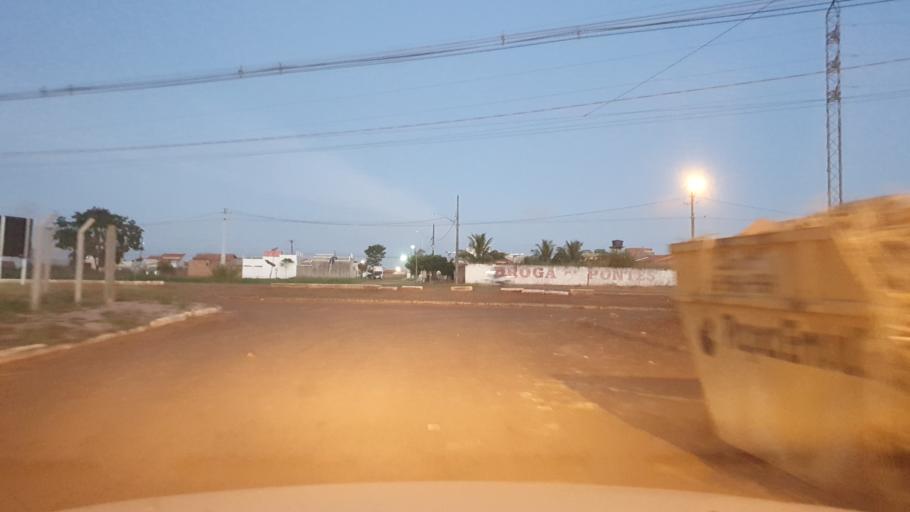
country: BR
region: Mato Grosso
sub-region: Pontes E Lacerda
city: Pontes e Lacerda
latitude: -15.2483
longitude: -59.3230
